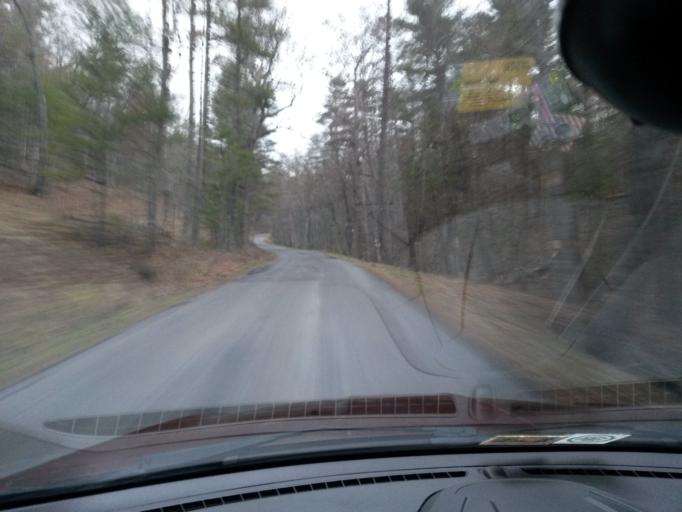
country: US
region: Virginia
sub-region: Bath County
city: Warm Springs
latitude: 38.0130
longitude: -79.7125
